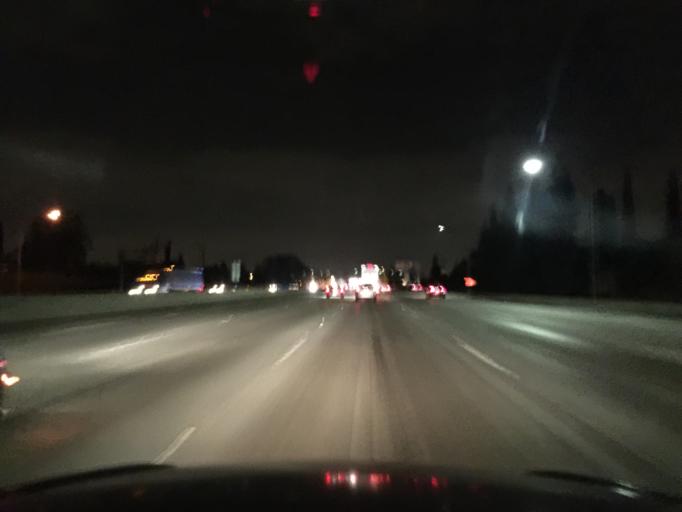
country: US
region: California
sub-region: Orange County
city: Placentia
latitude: 33.8404
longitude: -117.8760
